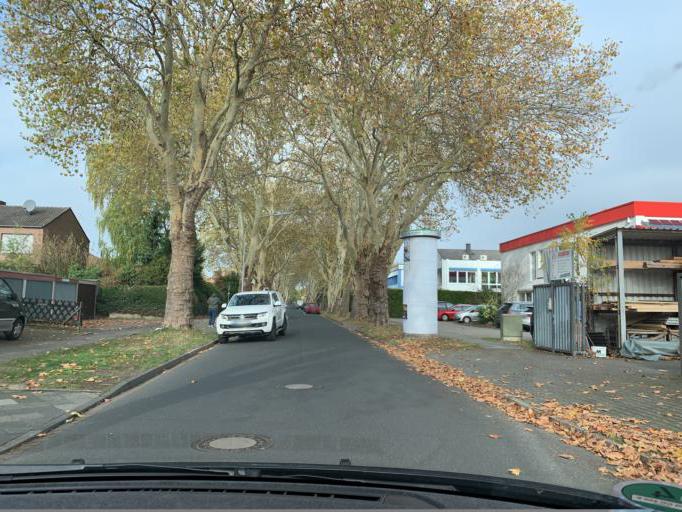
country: DE
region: North Rhine-Westphalia
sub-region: Regierungsbezirk Dusseldorf
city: Monchengladbach
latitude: 51.1369
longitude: 6.4115
